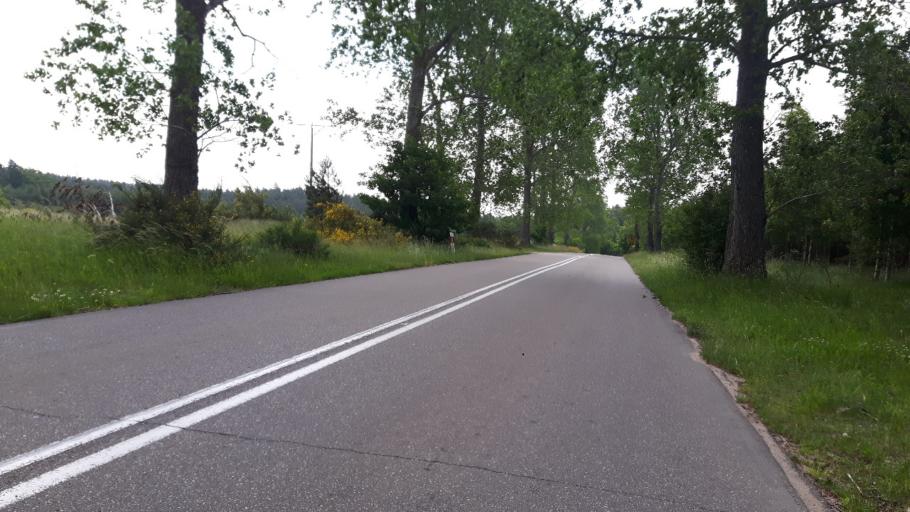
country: PL
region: Pomeranian Voivodeship
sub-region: Powiat leborski
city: Leba
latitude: 54.7537
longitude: 17.7099
